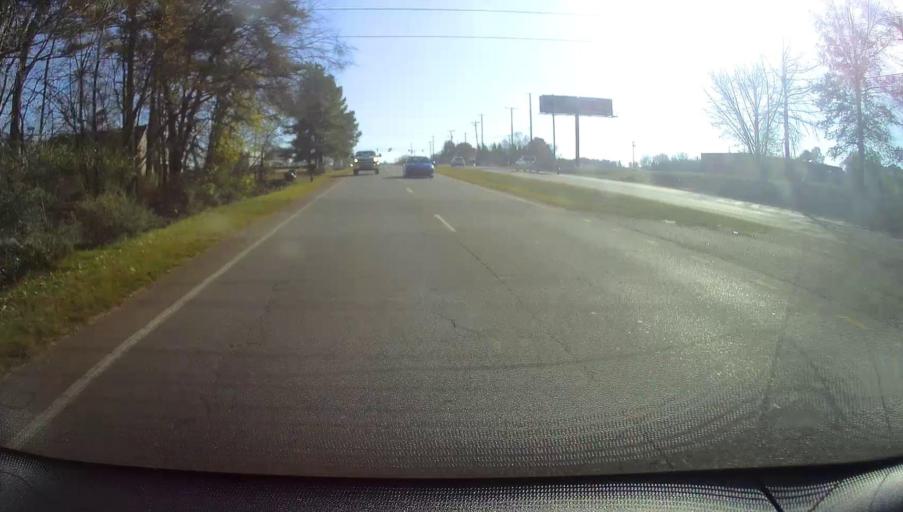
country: US
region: Alabama
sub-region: Limestone County
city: Athens
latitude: 34.7329
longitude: -86.9570
